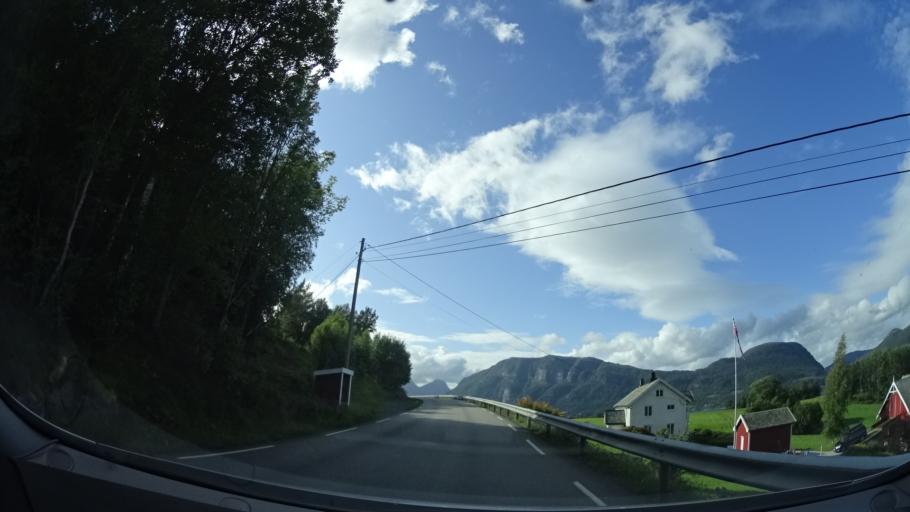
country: NO
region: More og Romsdal
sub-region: Halsa
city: Liaboen
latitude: 63.1387
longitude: 8.4278
